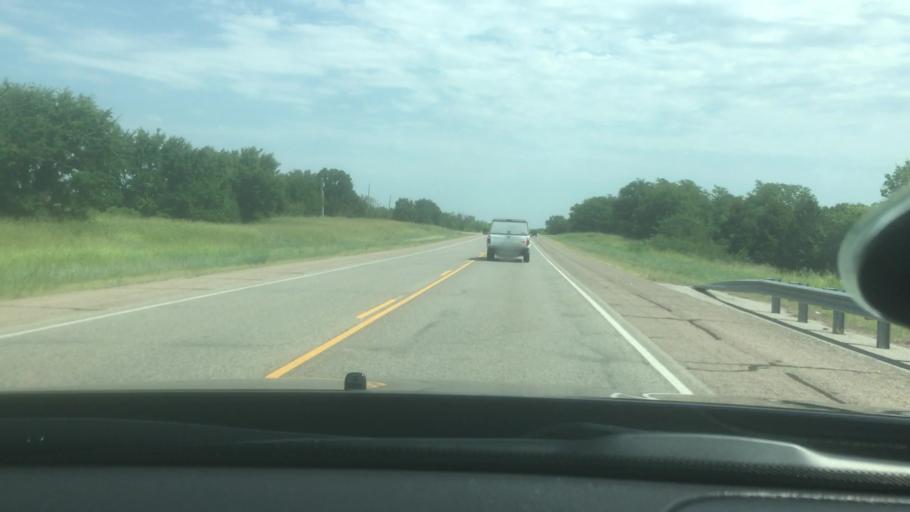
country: US
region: Oklahoma
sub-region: Seminole County
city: Maud
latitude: 35.0452
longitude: -96.9314
